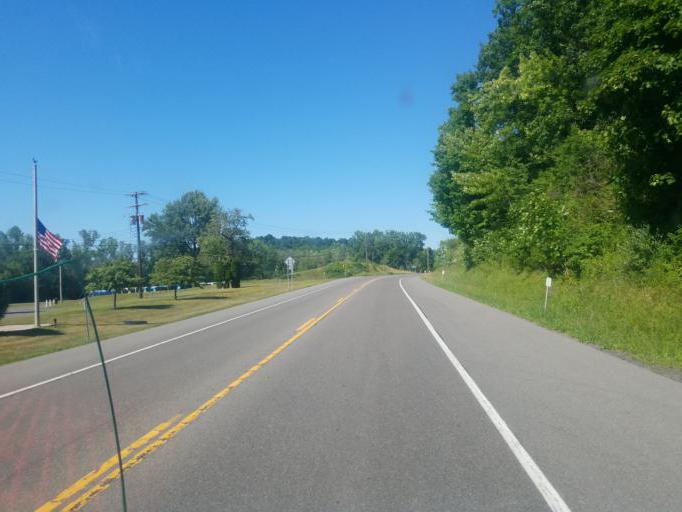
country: US
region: New York
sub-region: Wayne County
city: Lyons
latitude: 43.0662
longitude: -77.0382
